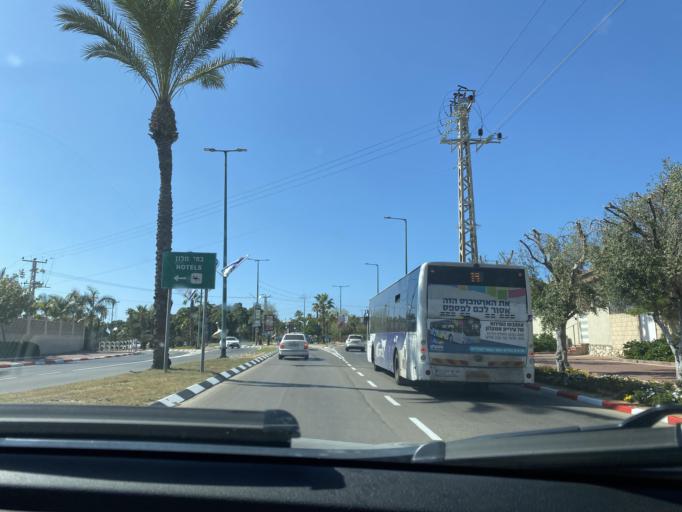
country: IL
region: Southern District
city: Ashqelon
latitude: 31.6798
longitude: 34.5741
